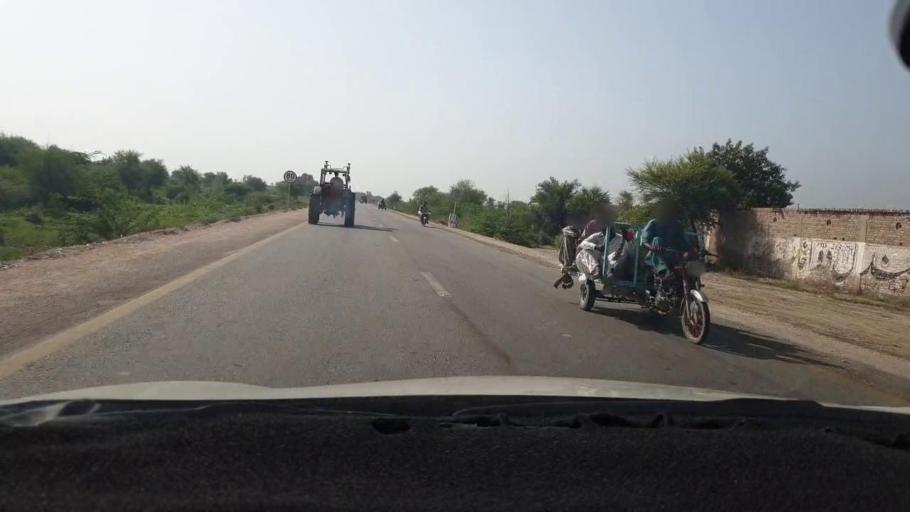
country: PK
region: Sindh
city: Sanghar
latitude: 26.0053
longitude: 68.9608
